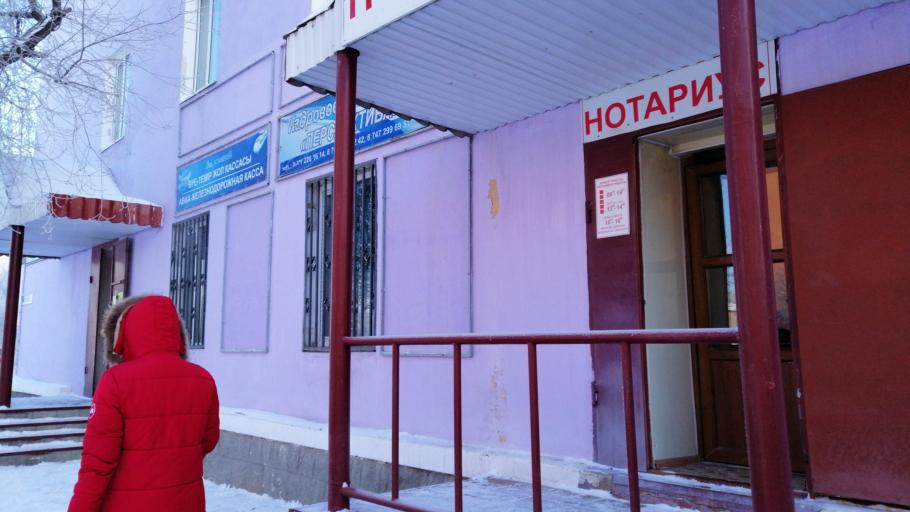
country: KZ
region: Aqtoebe
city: Aqtobe
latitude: 50.3110
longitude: 57.1469
